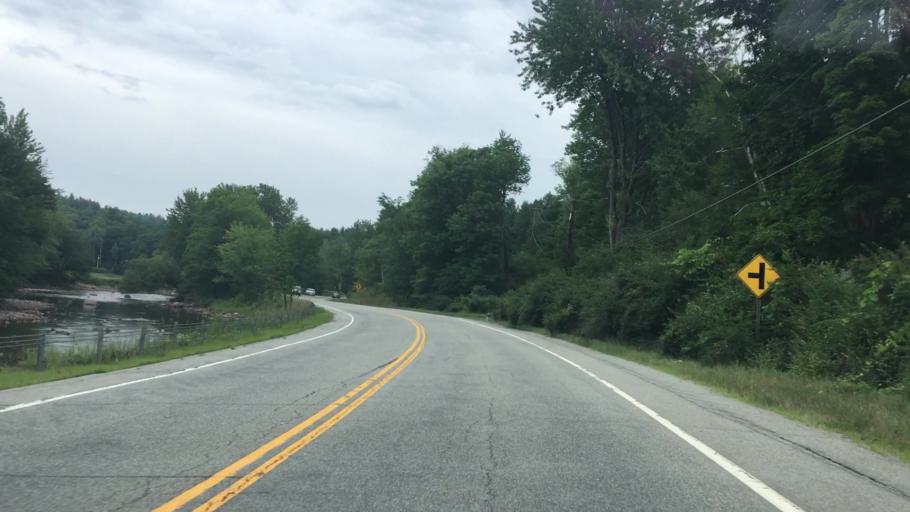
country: US
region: New York
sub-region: Essex County
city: Lake Placid
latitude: 44.2763
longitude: -73.7898
